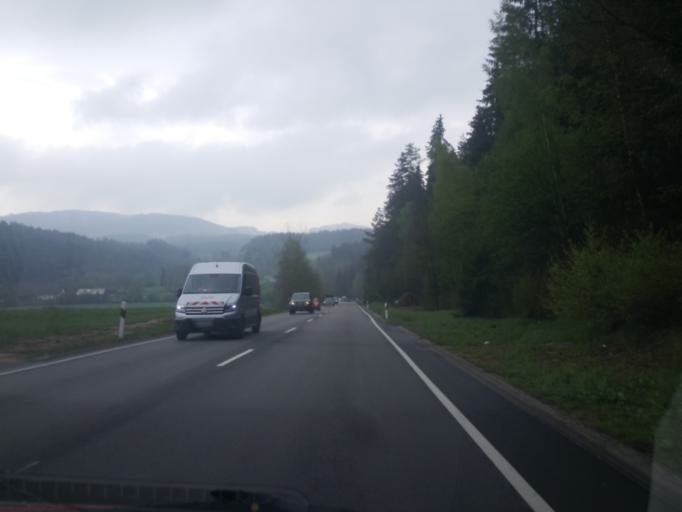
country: DE
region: Bavaria
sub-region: Lower Bavaria
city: Viechtach
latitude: 49.0596
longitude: 12.9081
